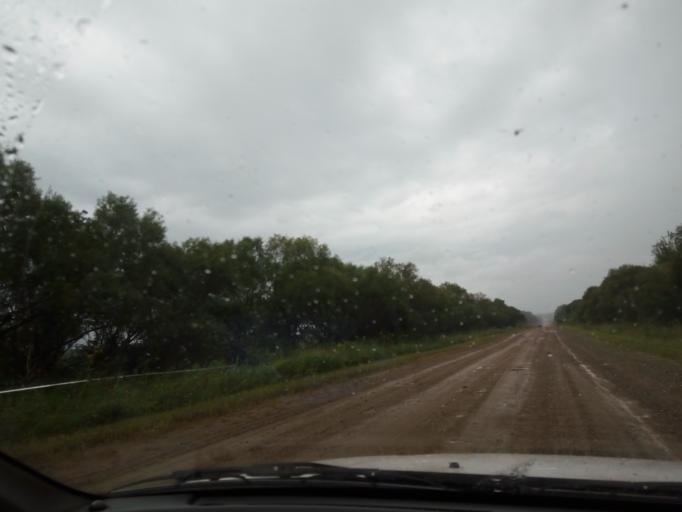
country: RU
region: Primorskiy
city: Lazo
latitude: 45.8437
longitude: 133.6444
